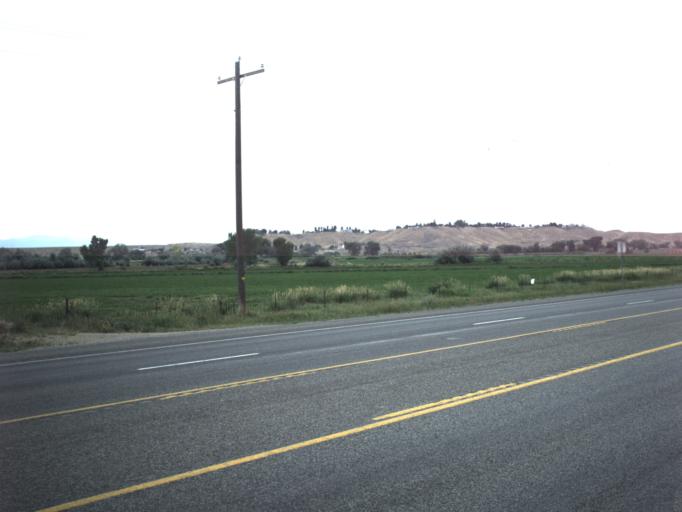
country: US
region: Utah
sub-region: Carbon County
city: Price
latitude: 39.5680
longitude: -110.7774
